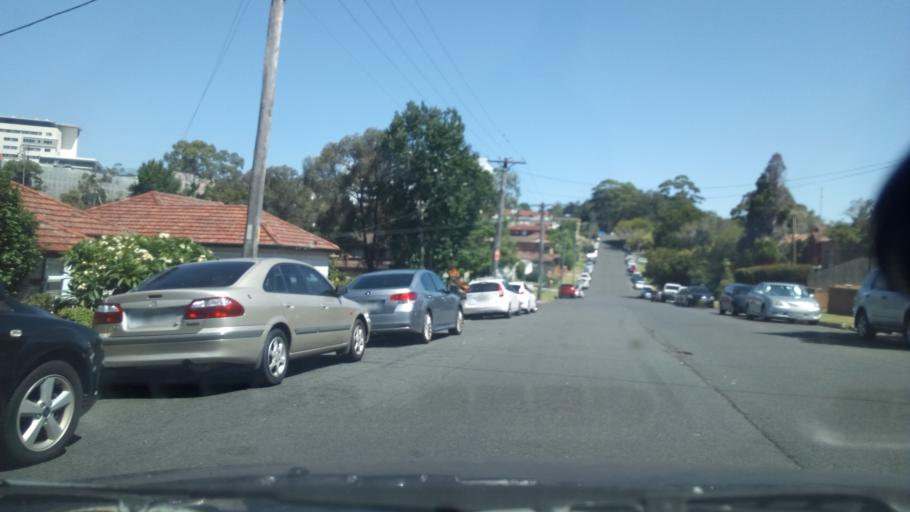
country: AU
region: New South Wales
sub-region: Wollongong
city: Gwynneville
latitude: -34.4223
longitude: 150.8804
